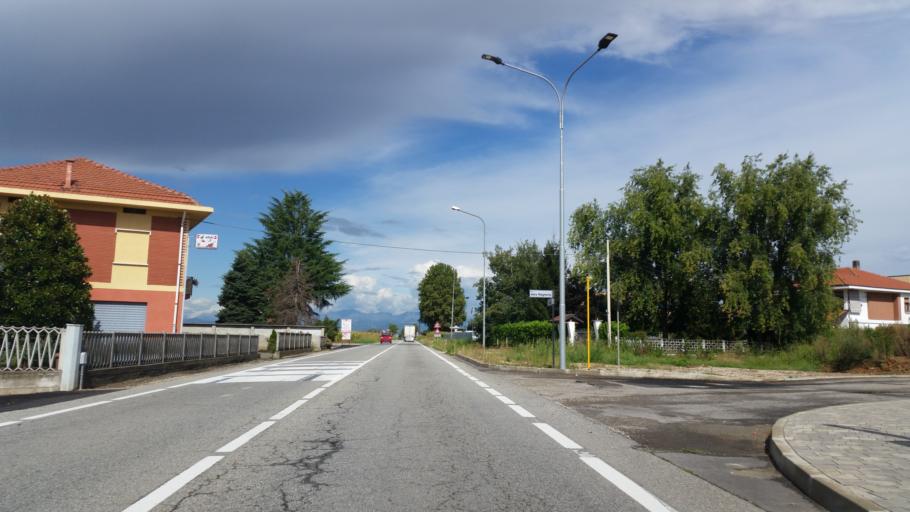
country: IT
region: Piedmont
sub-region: Provincia di Torino
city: Marocchi
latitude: 44.9437
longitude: 7.8137
